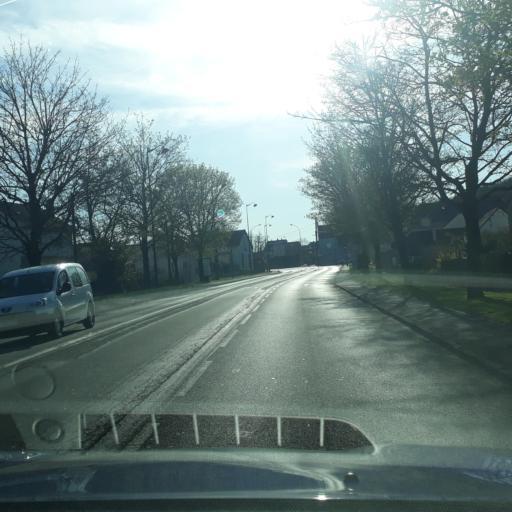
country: FR
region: Ile-de-France
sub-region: Departement de l'Essonne
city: Morigny-Champigny
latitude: 48.4334
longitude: 2.1737
